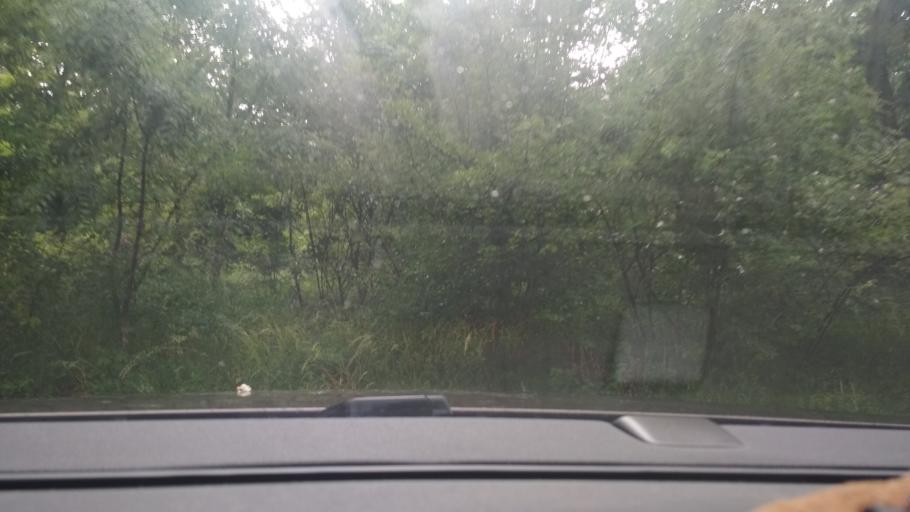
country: MD
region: Singerei
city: Biruinta
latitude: 47.7510
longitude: 28.1387
